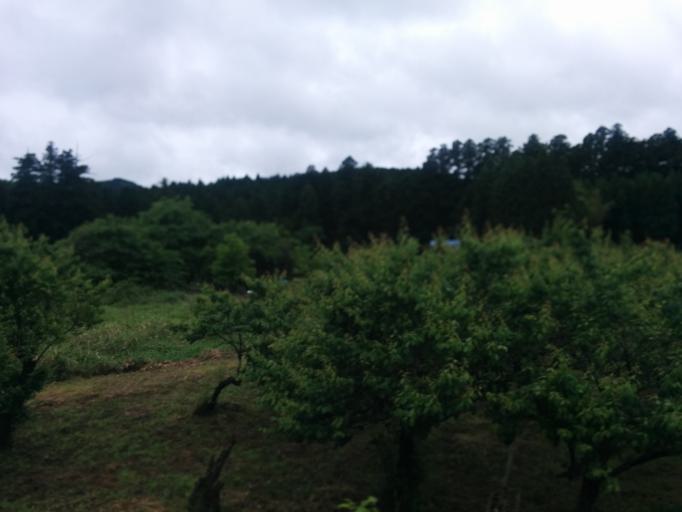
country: JP
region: Tochigi
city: Imaichi
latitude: 36.7090
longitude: 139.7030
